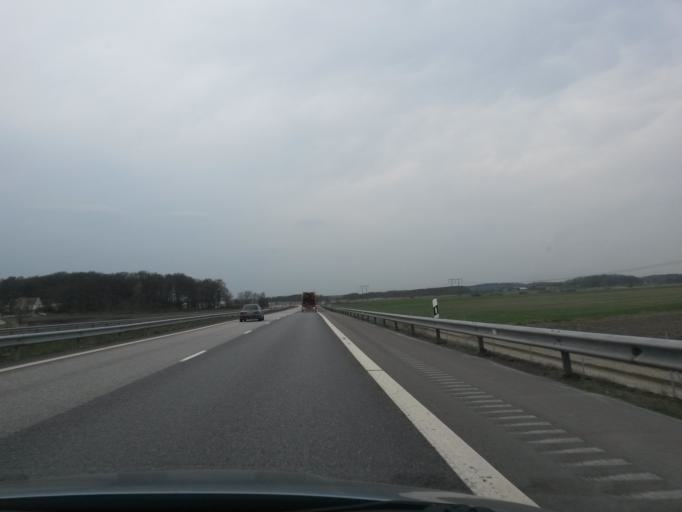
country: SE
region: Halland
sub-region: Varbergs Kommun
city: Traslovslage
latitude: 57.1061
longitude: 12.3351
